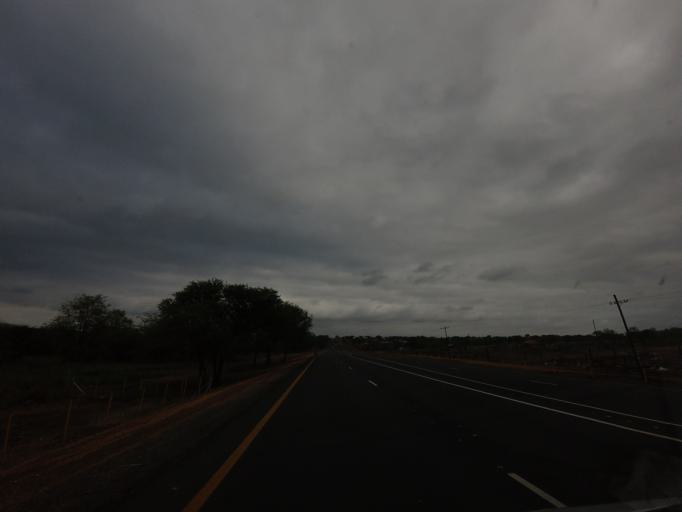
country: ZA
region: Mpumalanga
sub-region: Ehlanzeni District
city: Komatipoort
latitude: -25.4434
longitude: 31.6891
